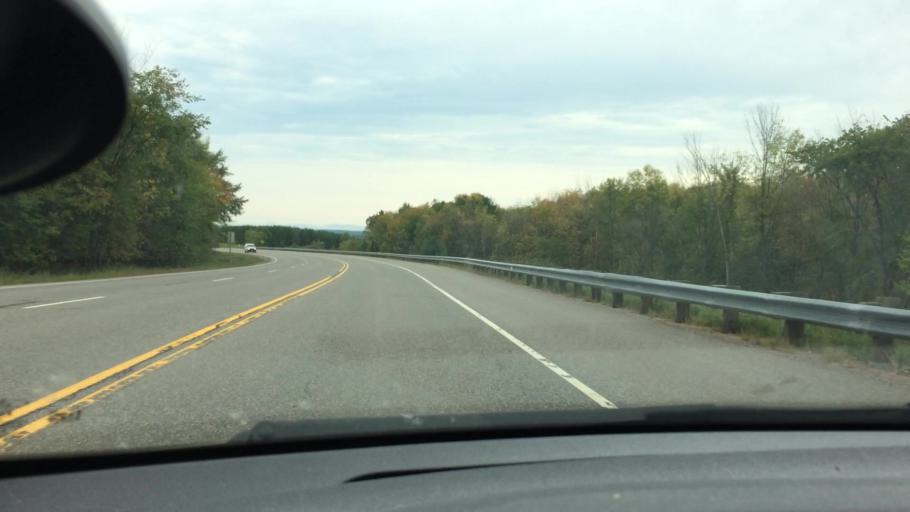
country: US
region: Wisconsin
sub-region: Clark County
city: Neillsville
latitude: 44.5656
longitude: -90.6619
